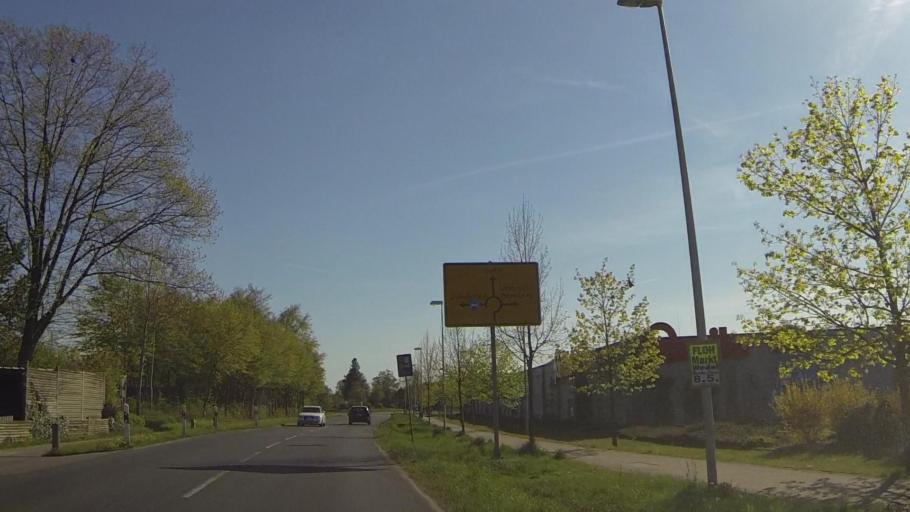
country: DE
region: Schleswig-Holstein
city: Pinneberg
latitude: 53.6464
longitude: 9.7727
